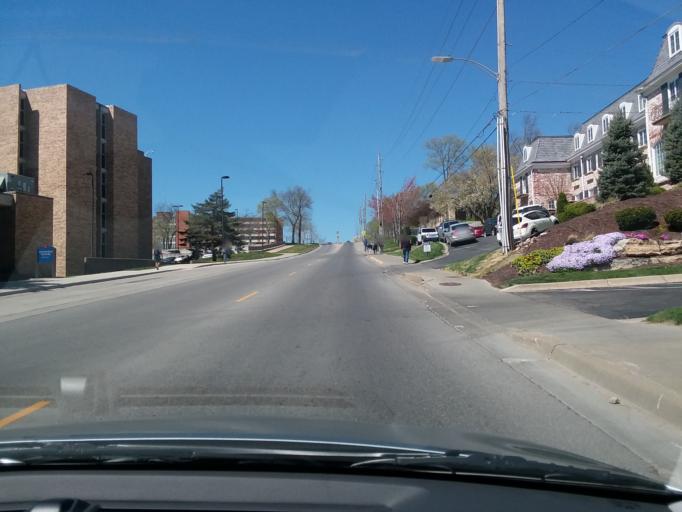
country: US
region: Kansas
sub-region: Douglas County
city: Lawrence
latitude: 38.9571
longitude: -95.2554
